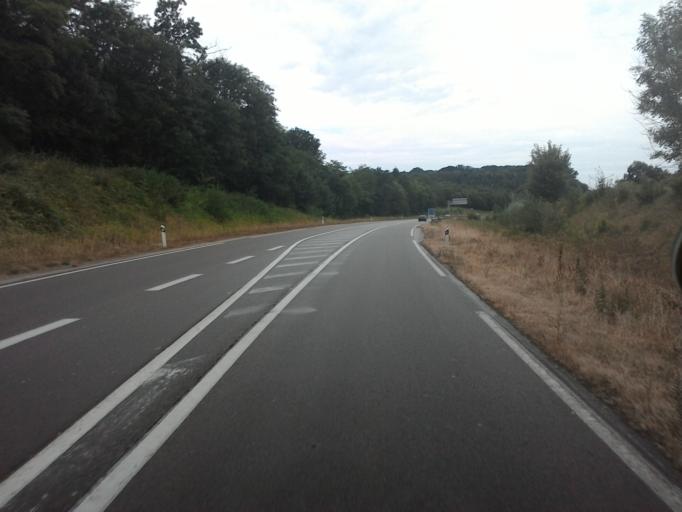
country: FR
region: Franche-Comte
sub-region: Departement du Jura
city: Poligny
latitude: 46.8373
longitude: 5.6814
